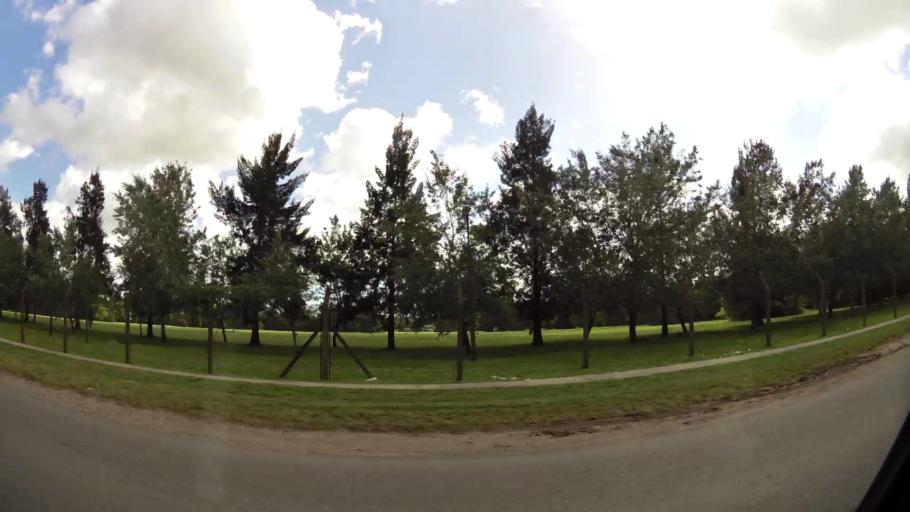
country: AR
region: Buenos Aires
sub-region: Partido de Quilmes
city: Quilmes
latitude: -34.8294
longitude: -58.1779
